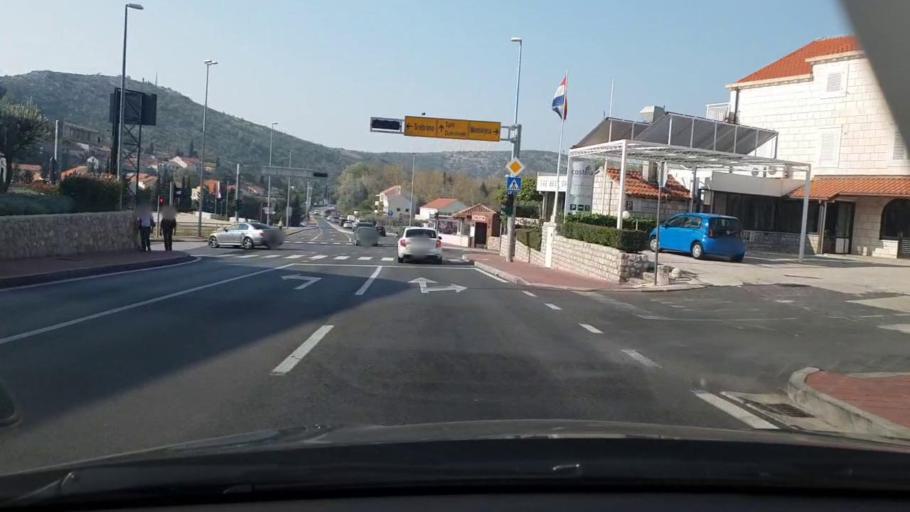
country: HR
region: Dubrovacko-Neretvanska
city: Cibaca
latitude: 42.6251
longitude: 18.1930
